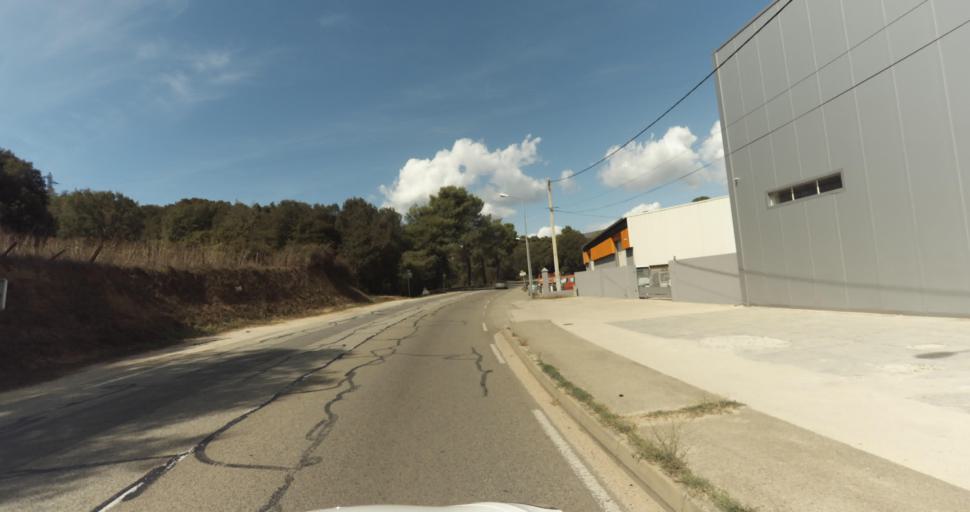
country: FR
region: Corsica
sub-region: Departement de la Corse-du-Sud
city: Afa
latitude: 41.9588
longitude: 8.7805
